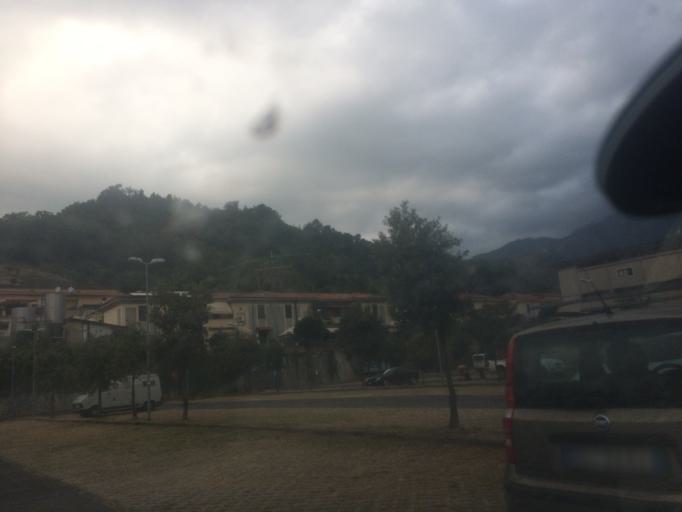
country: IT
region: Tuscany
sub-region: Provincia di Massa-Carrara
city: Carrara
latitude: 44.0739
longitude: 10.0915
